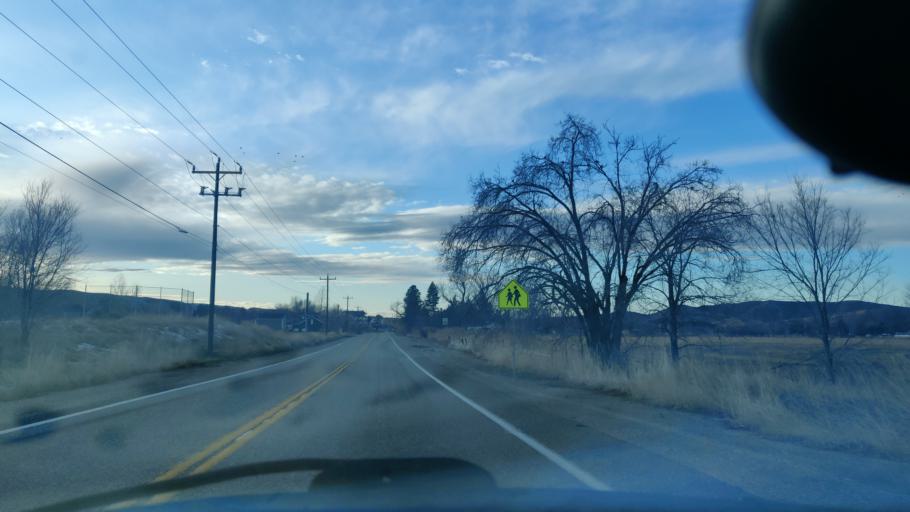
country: US
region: Idaho
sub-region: Ada County
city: Eagle
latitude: 43.7277
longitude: -116.2544
